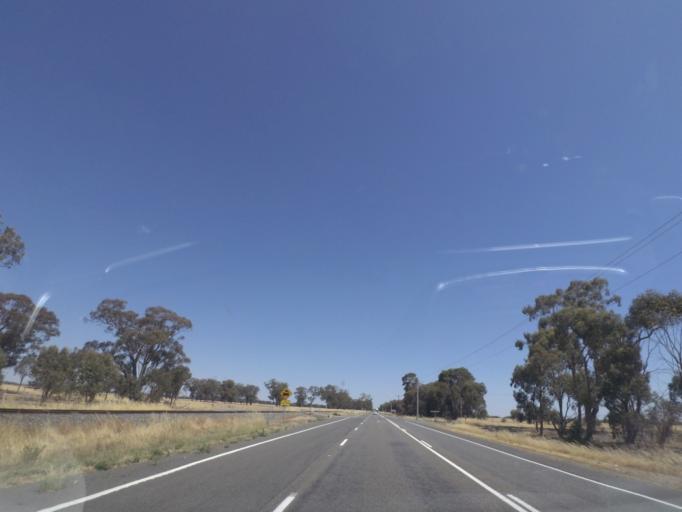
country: AU
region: Victoria
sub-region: Greater Shepparton
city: Shepparton
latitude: -36.1984
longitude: 145.4318
